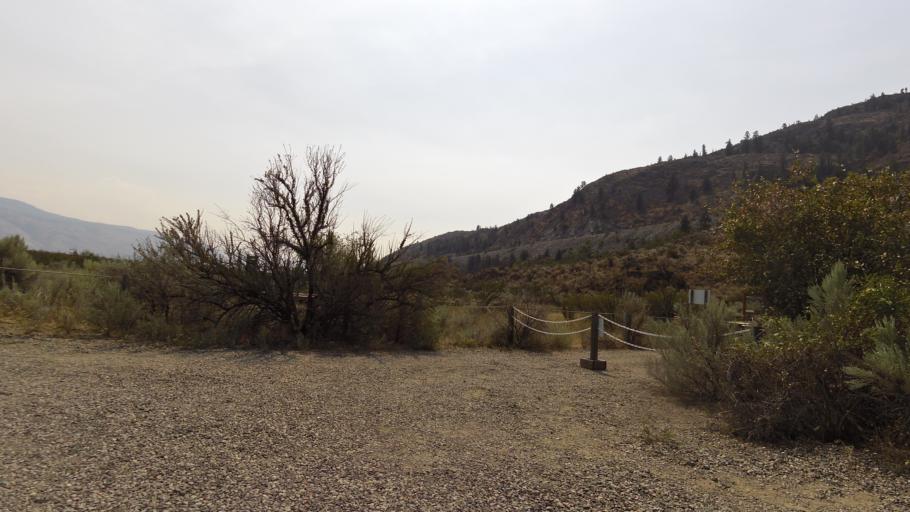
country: CA
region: British Columbia
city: Osoyoos
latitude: 49.0539
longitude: -119.5199
